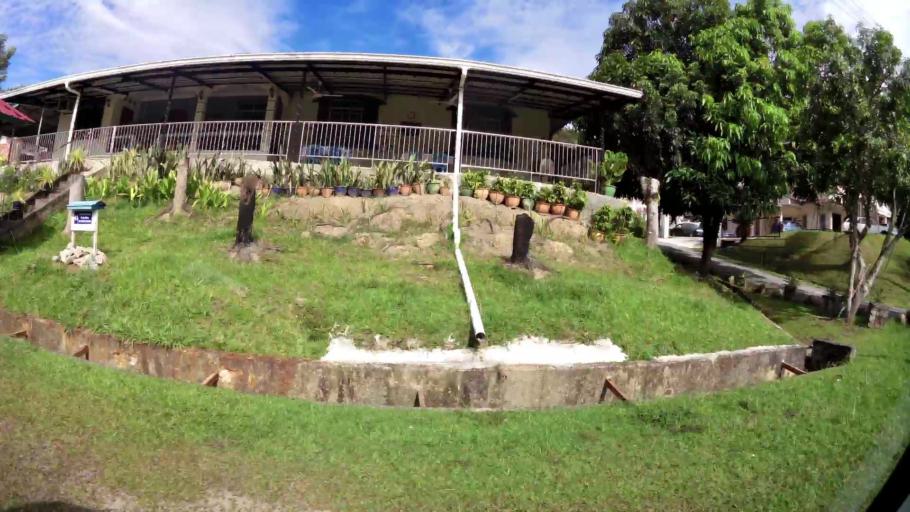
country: BN
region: Brunei and Muara
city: Bandar Seri Begawan
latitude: 4.9209
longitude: 114.8970
